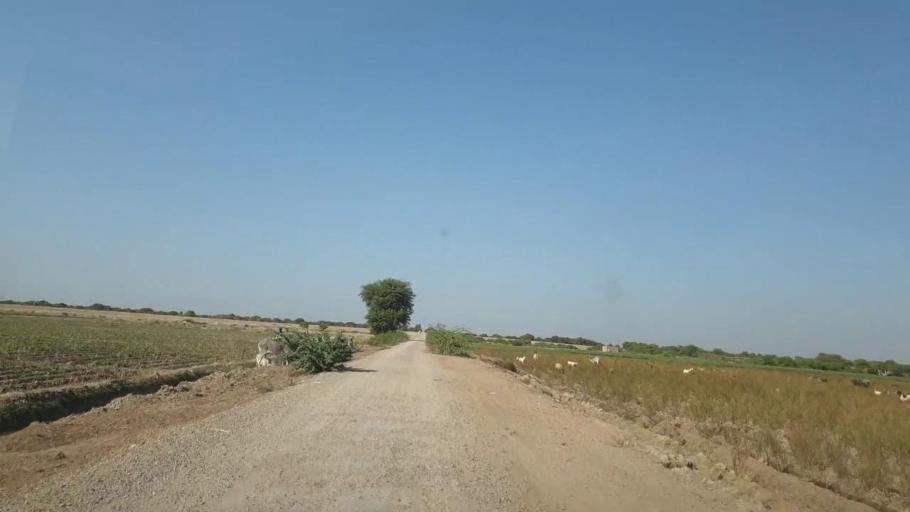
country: PK
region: Sindh
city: Nabisar
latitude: 25.0299
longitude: 69.4866
